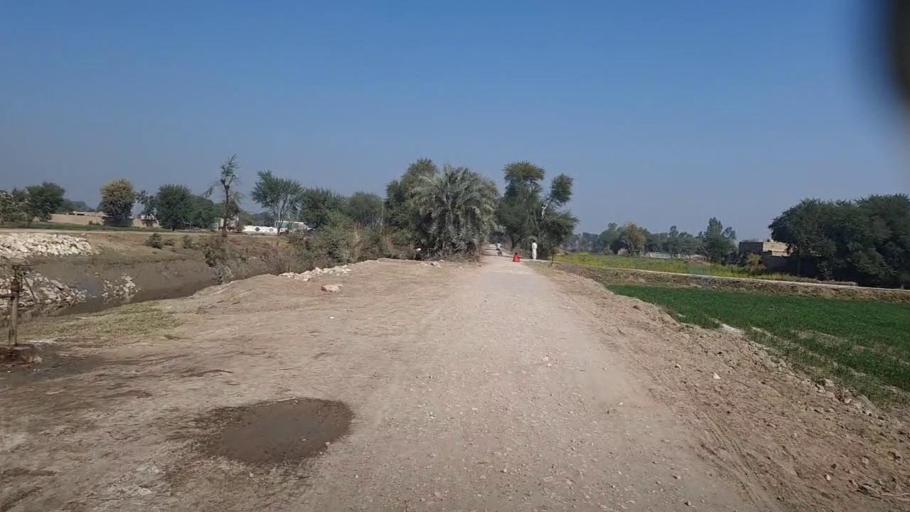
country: PK
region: Sindh
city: Khairpur
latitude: 27.9749
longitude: 69.7089
